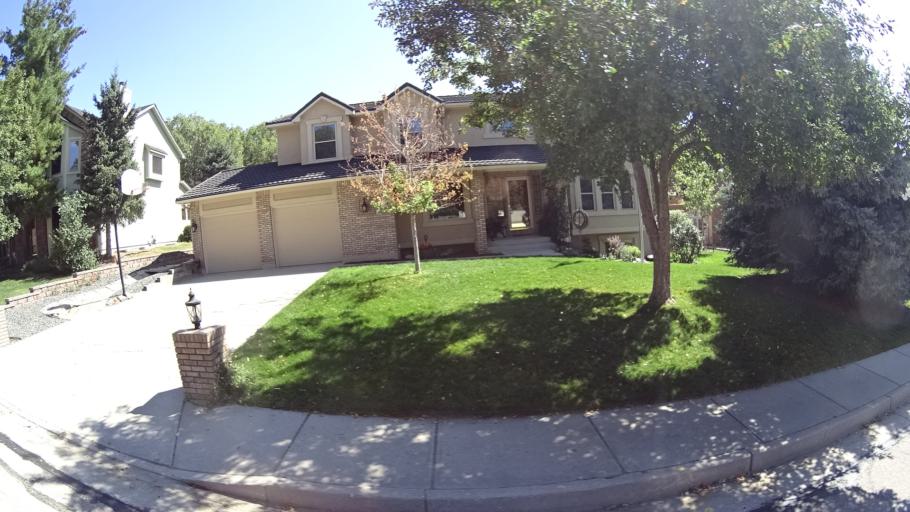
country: US
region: Colorado
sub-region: El Paso County
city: Cimarron Hills
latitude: 38.9134
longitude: -104.7529
